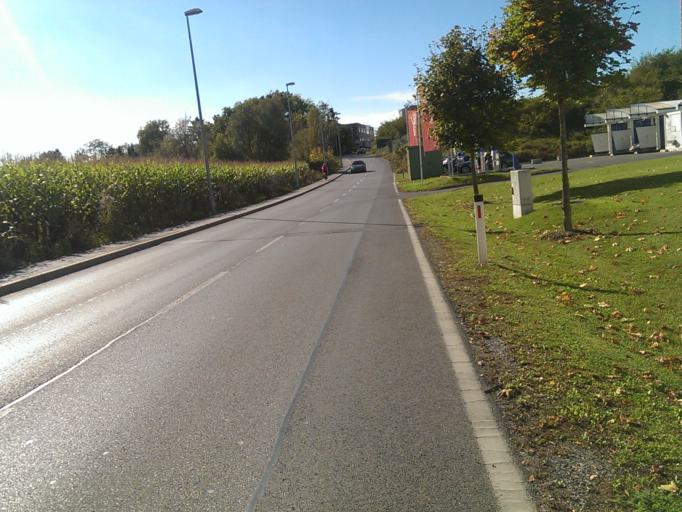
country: AT
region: Styria
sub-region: Politischer Bezirk Graz-Umgebung
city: Feldkirchen bei Graz
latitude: 47.0298
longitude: 15.4381
